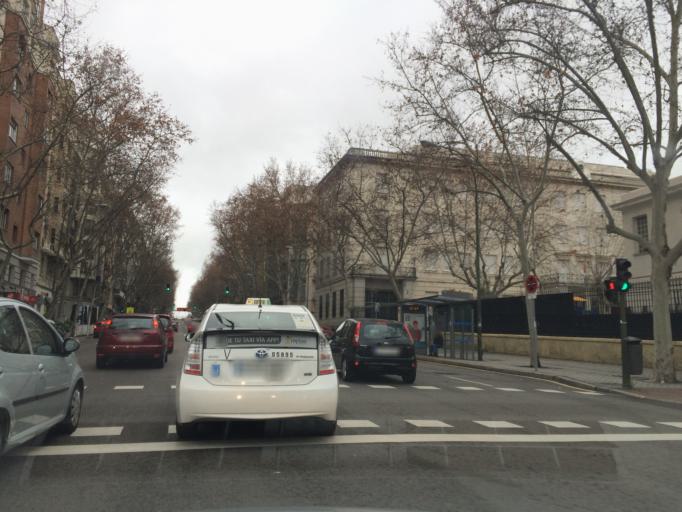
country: ES
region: Madrid
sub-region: Provincia de Madrid
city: Chamberi
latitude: 40.4416
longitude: -3.6950
